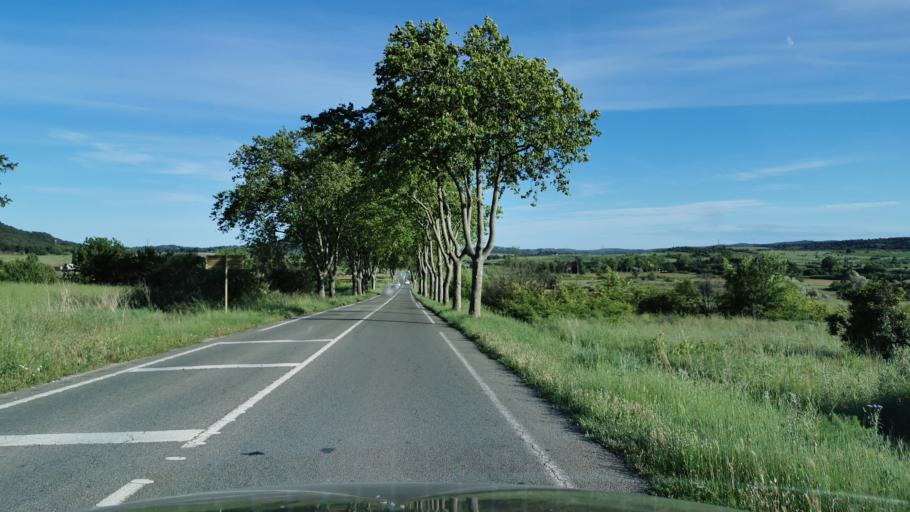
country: FR
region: Languedoc-Roussillon
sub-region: Departement de l'Aude
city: Marcorignan
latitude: 43.2219
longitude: 2.9249
